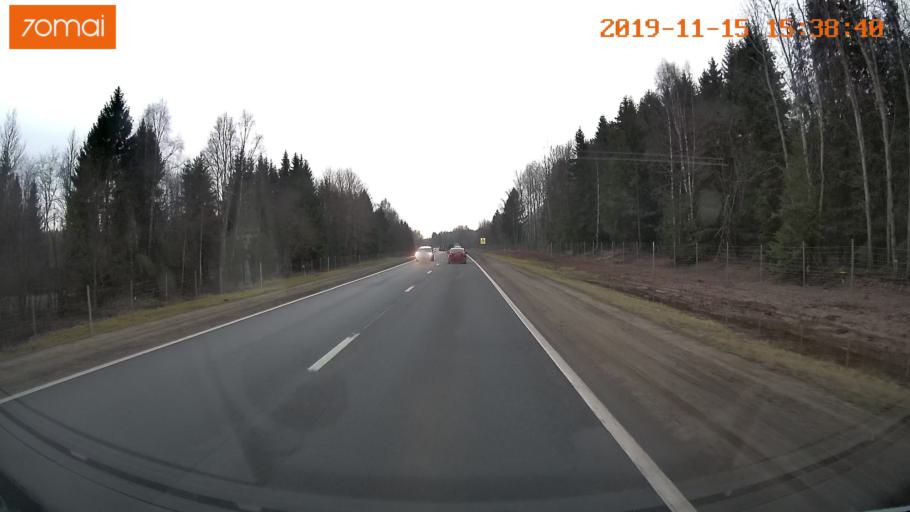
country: RU
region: Jaroslavl
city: Danilov
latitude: 58.0278
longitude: 40.0778
